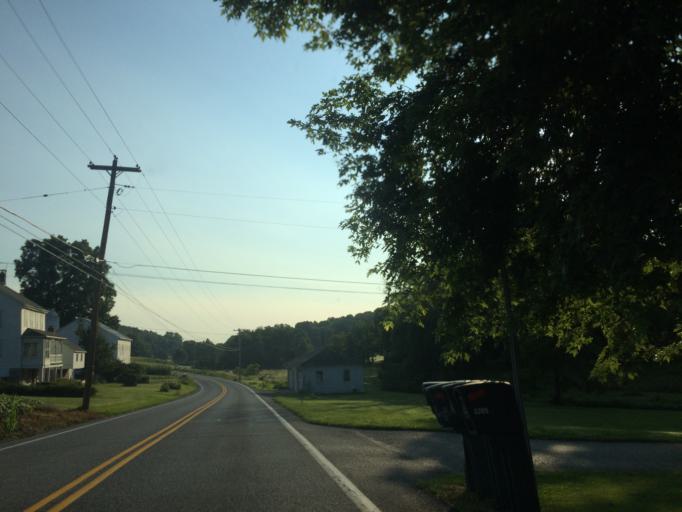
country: US
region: Pennsylvania
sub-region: York County
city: Glen Rock
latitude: 39.7652
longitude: -76.7631
